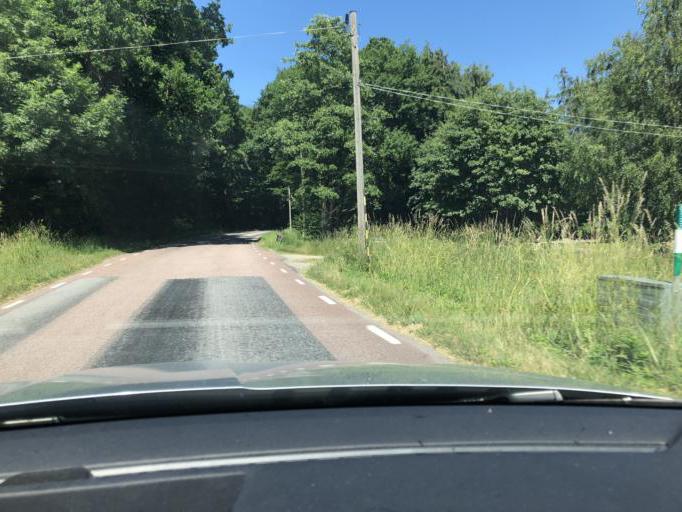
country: SE
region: Blekinge
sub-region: Solvesborgs Kommun
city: Soelvesborg
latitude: 56.1383
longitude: 14.6074
